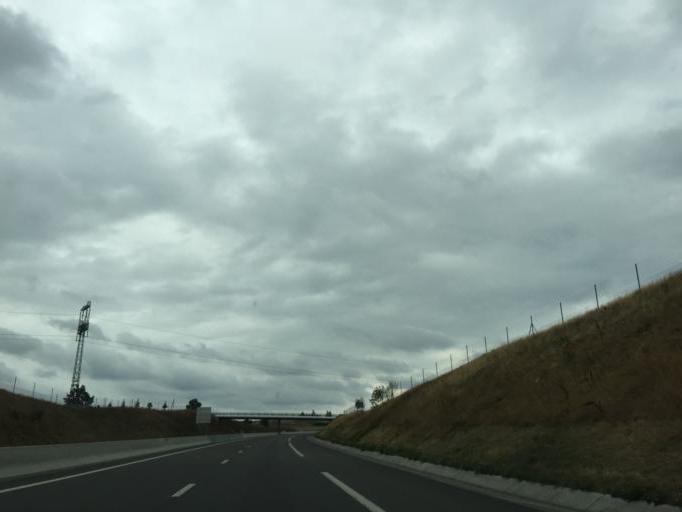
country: FR
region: Rhone-Alpes
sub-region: Departement de la Loire
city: Balbigny
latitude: 45.8394
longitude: 4.1790
